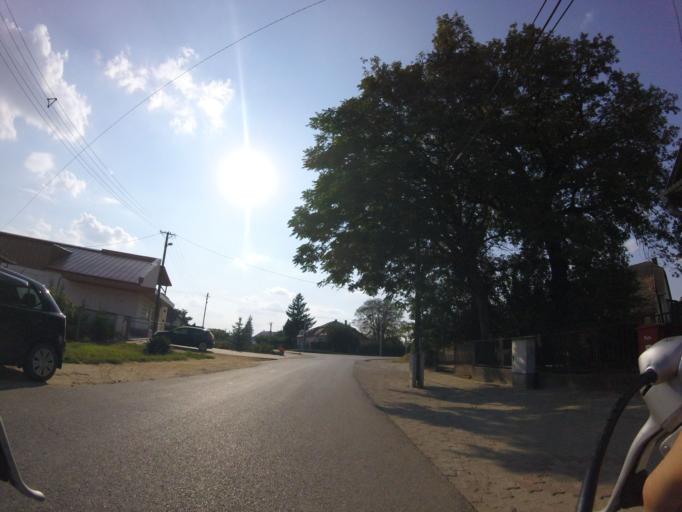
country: HU
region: Szabolcs-Szatmar-Bereg
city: Nyirkarasz
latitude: 48.0965
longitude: 22.1005
